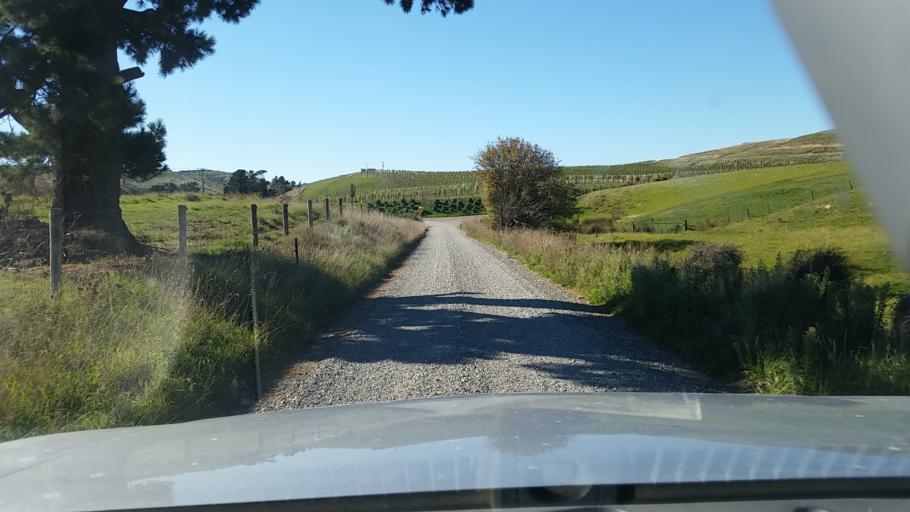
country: NZ
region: Marlborough
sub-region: Marlborough District
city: Blenheim
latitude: -41.6741
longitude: 174.1463
